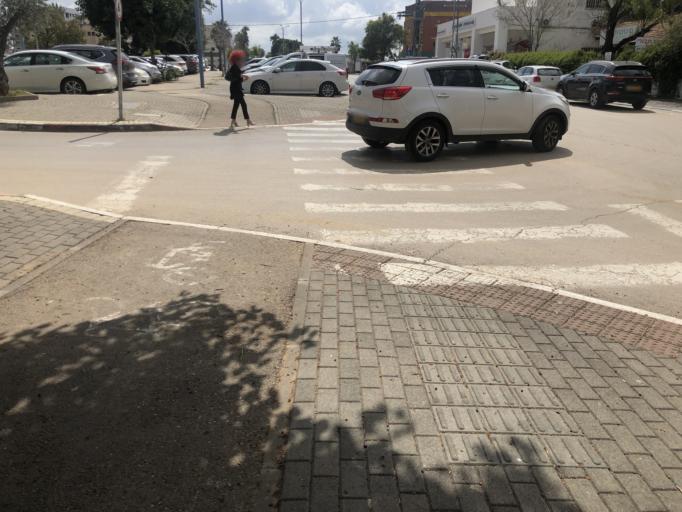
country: IL
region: Haifa
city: Hadera
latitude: 32.4757
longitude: 34.9723
